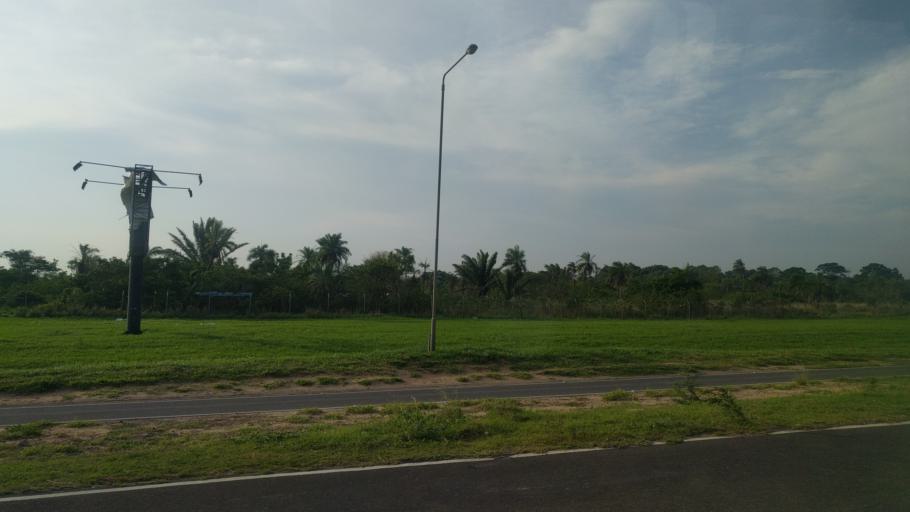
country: BO
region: Santa Cruz
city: La Belgica
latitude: -17.6574
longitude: -63.1567
